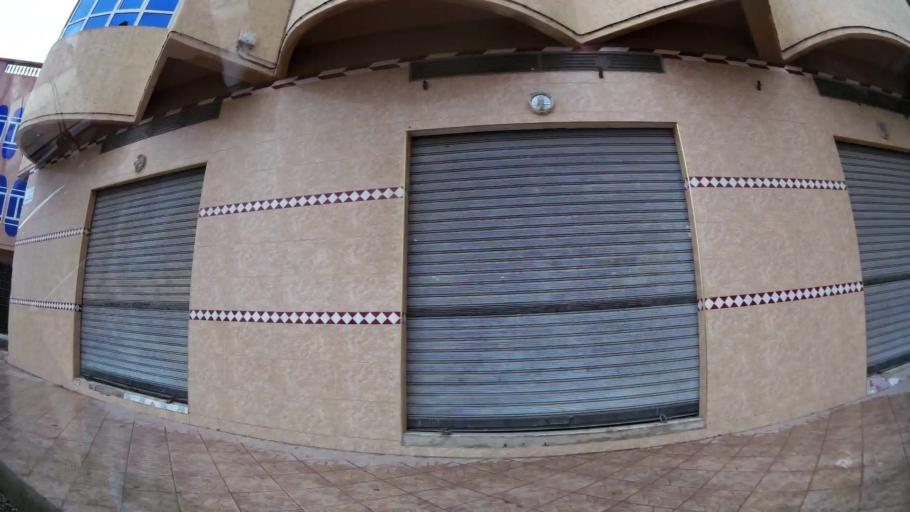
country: MA
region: Oriental
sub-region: Nador
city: Nador
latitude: 35.1717
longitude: -2.9413
